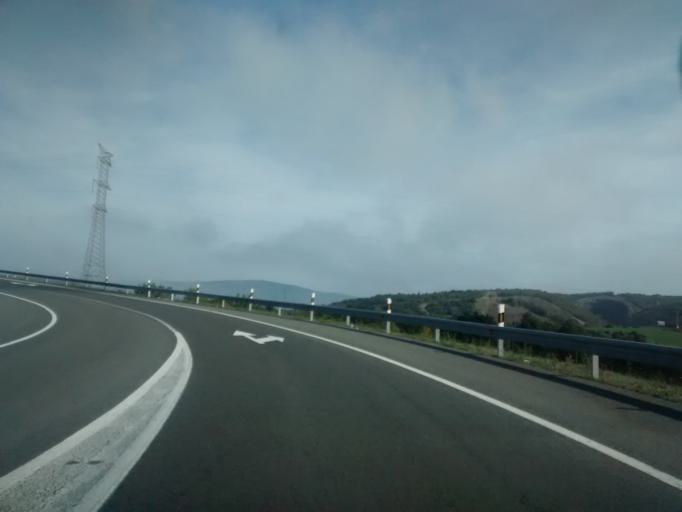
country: ES
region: Basque Country
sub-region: Provincia de Alava
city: Gasteiz / Vitoria
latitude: 42.9291
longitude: -2.6425
